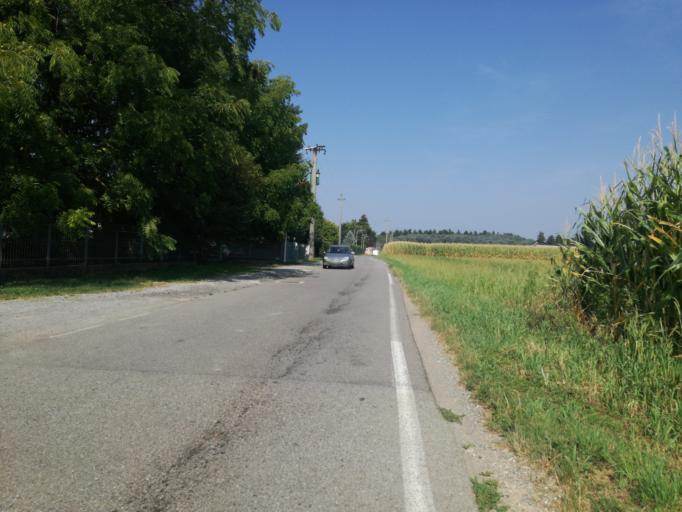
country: IT
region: Lombardy
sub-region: Provincia di Monza e Brianza
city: Cornate d'Adda
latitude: 45.6267
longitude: 9.4834
